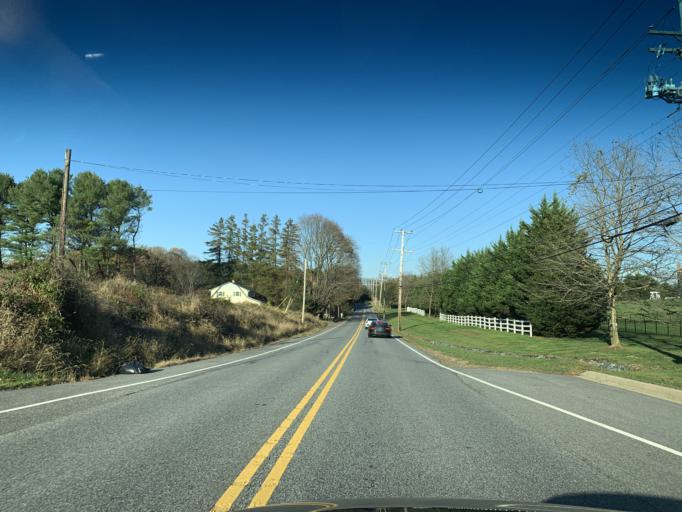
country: US
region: Maryland
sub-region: Harford County
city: Jarrettsville
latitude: 39.5470
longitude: -76.4717
